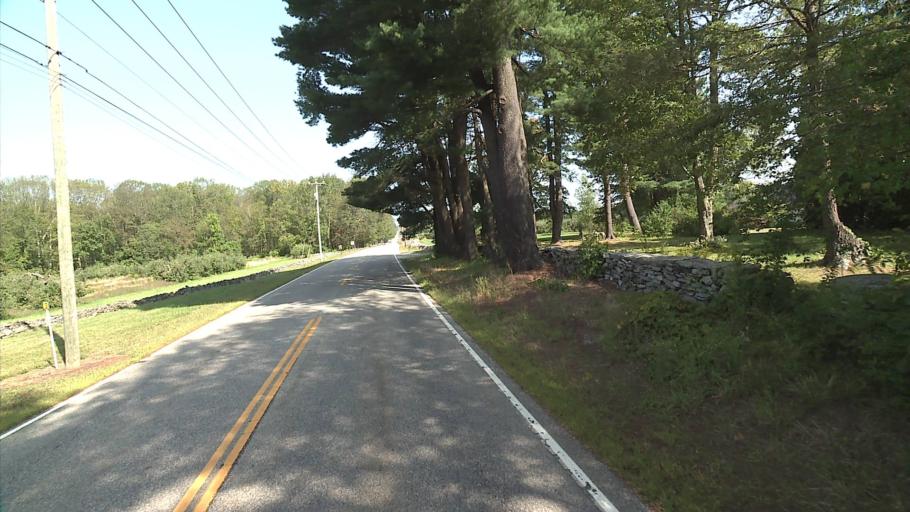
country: US
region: Connecticut
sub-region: Windham County
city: East Brooklyn
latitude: 41.8255
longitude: -71.9587
